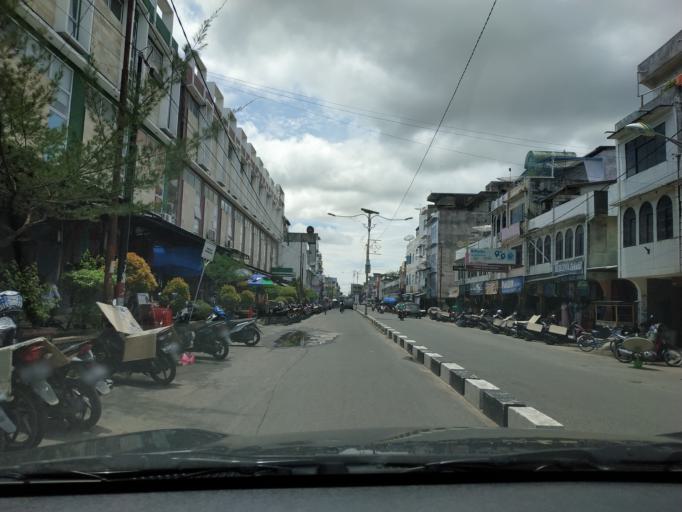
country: ID
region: Riau
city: Tembilahan
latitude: -0.3278
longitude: 103.1580
